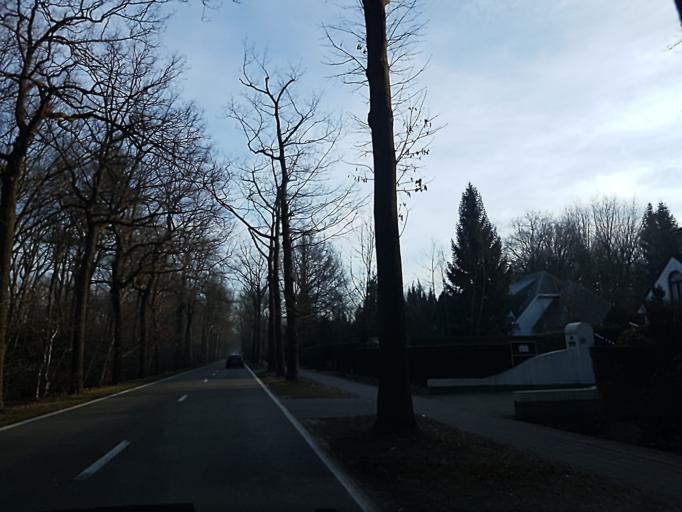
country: BE
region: Flanders
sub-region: Provincie Antwerpen
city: Schilde
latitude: 51.2488
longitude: 4.6236
